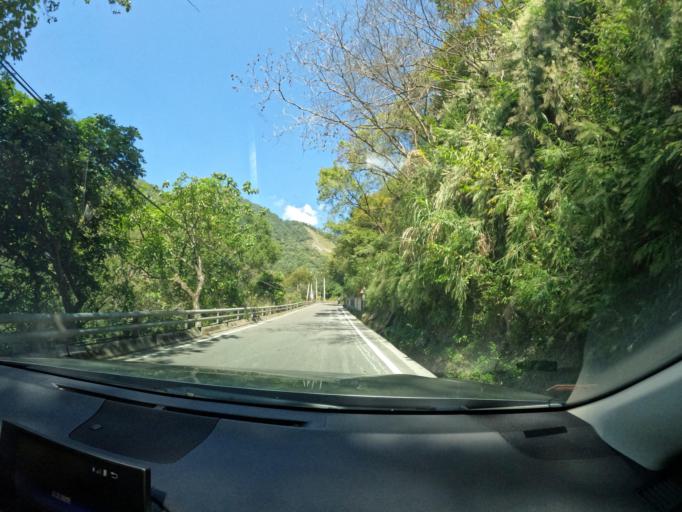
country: TW
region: Taiwan
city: Yujing
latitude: 23.2376
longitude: 120.8118
